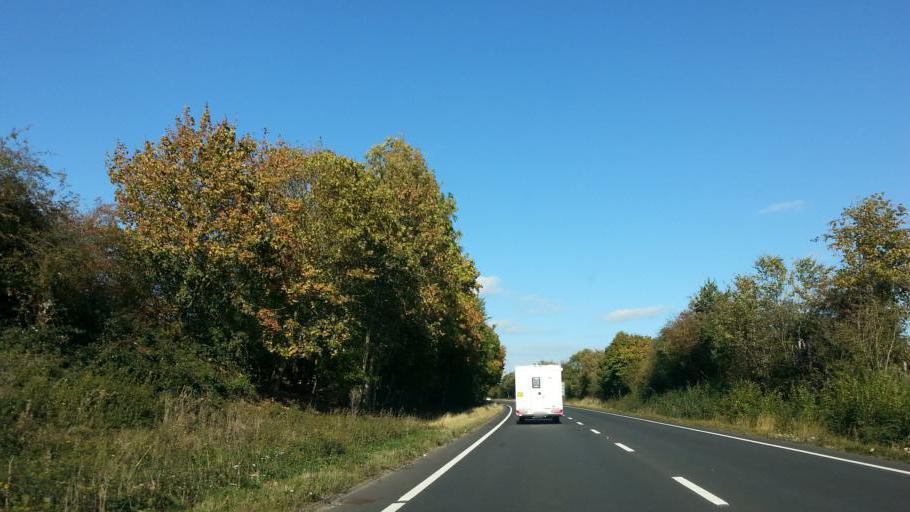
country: GB
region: England
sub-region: Northamptonshire
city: Oundle
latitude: 52.4740
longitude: -0.4569
